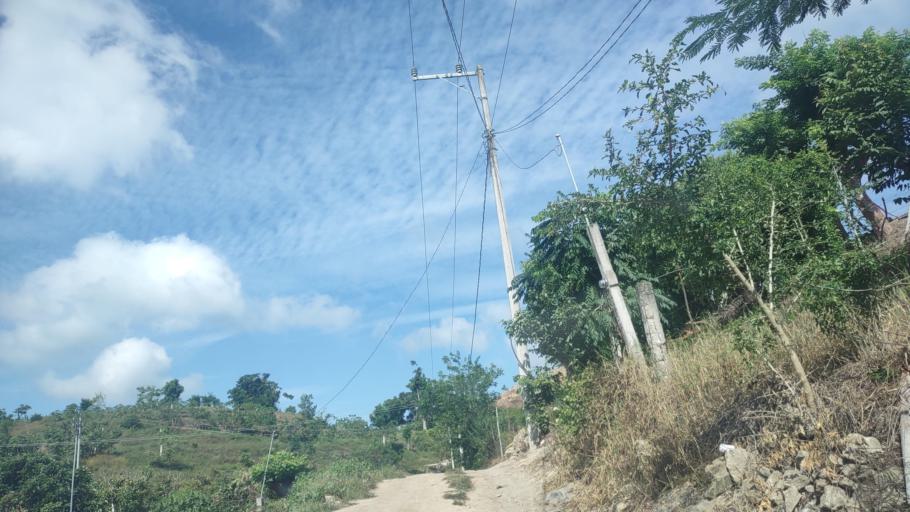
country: MM
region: Shan
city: Taunggyi
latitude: 20.5875
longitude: 97.3731
